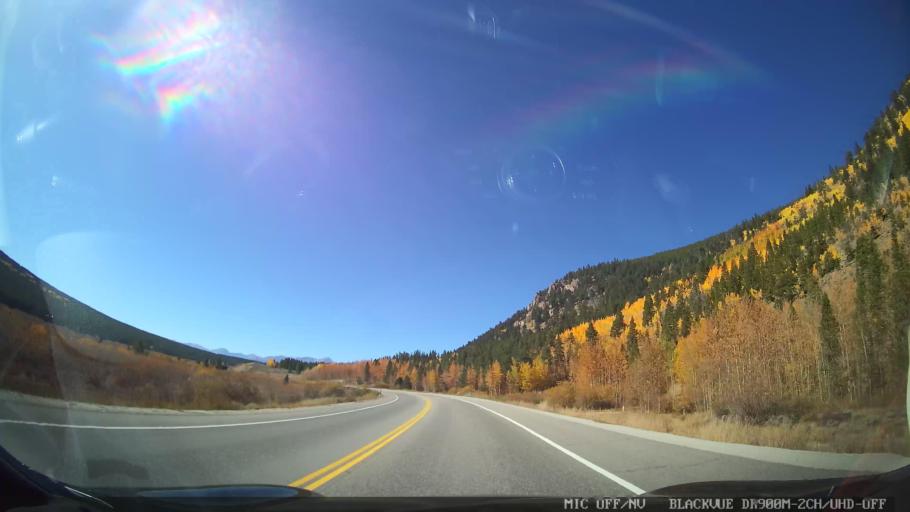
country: US
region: Colorado
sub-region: Lake County
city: Leadville North
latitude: 39.2922
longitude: -106.2781
